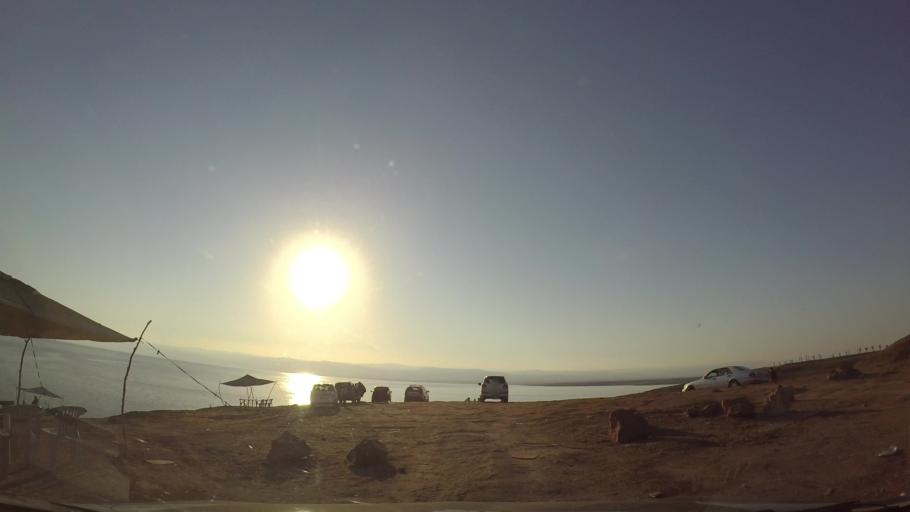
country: PS
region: West Bank
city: Jericho
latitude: 31.7474
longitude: 35.5898
